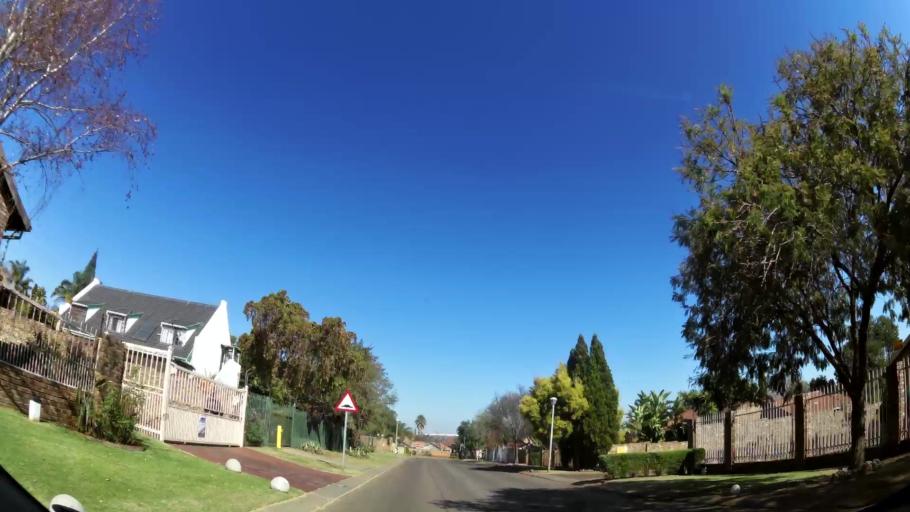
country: ZA
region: Gauteng
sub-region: City of Tshwane Metropolitan Municipality
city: Centurion
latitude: -25.8648
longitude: 28.1778
